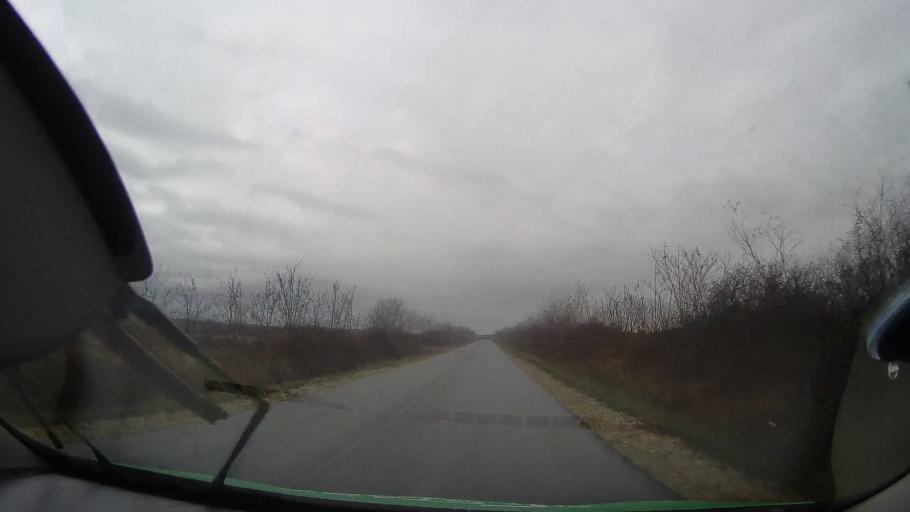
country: RO
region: Bihor
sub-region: Comuna Cociuba Mare
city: Cociuba Mare
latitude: 46.6990
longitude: 22.0335
